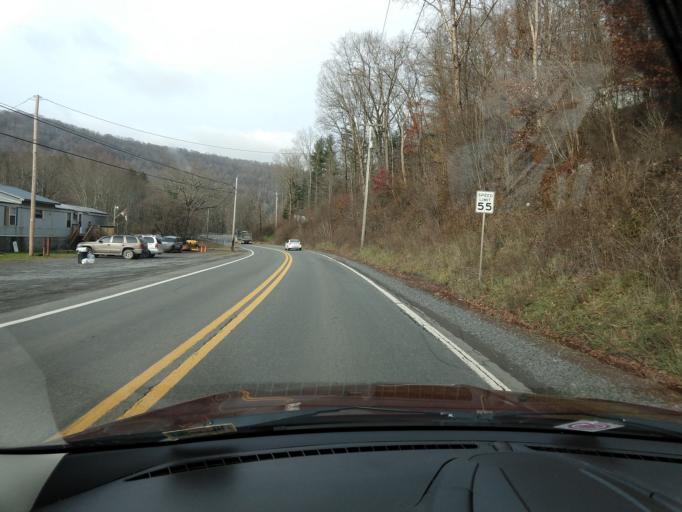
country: US
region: West Virginia
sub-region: Greenbrier County
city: Rainelle
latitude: 37.9868
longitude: -80.7267
